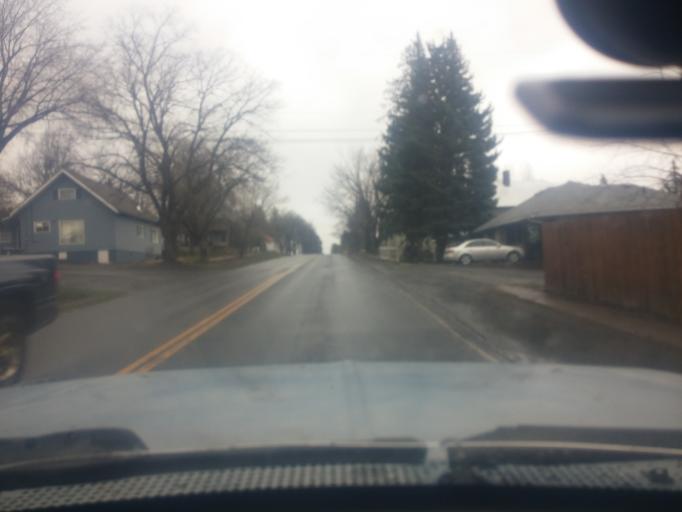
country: US
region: Idaho
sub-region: Latah County
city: Moscow
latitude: 46.9216
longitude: -116.8965
